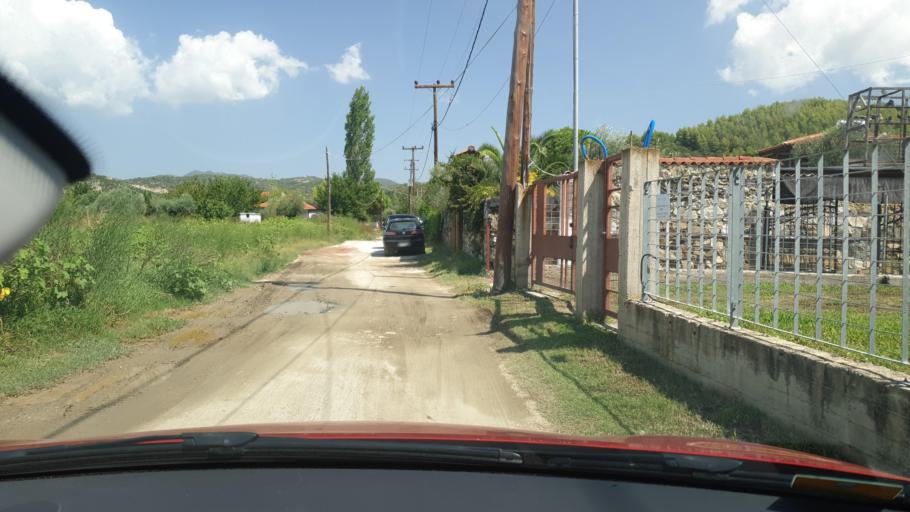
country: GR
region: Central Macedonia
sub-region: Nomos Chalkidikis
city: Sykia
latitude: 39.9794
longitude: 23.9084
